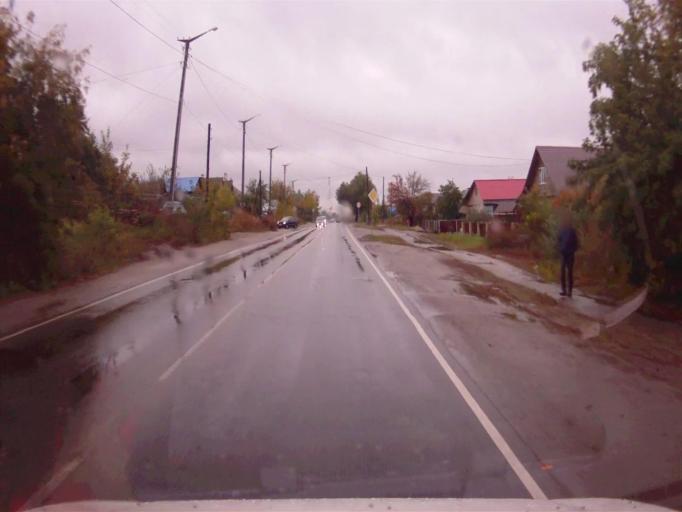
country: RU
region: Chelyabinsk
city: Kyshtym
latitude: 55.7117
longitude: 60.5578
